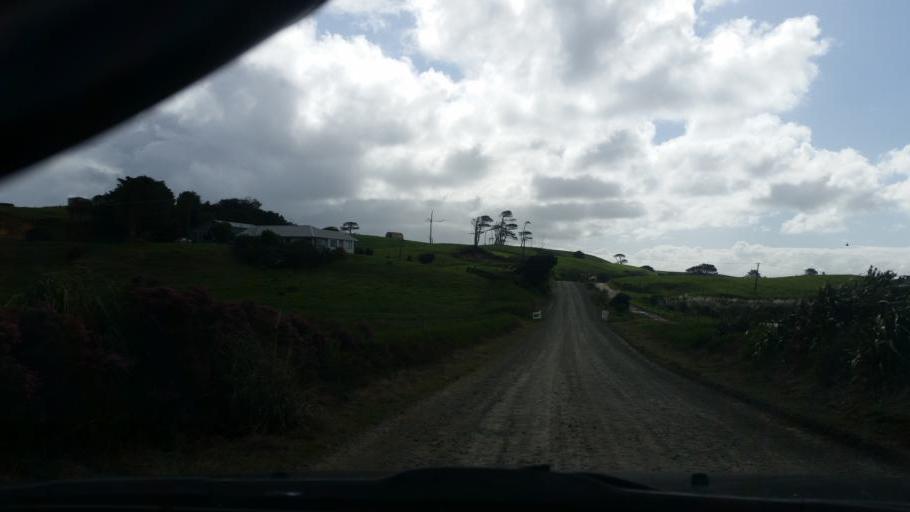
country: NZ
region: Northland
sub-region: Kaipara District
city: Dargaville
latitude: -36.0705
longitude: 173.8810
